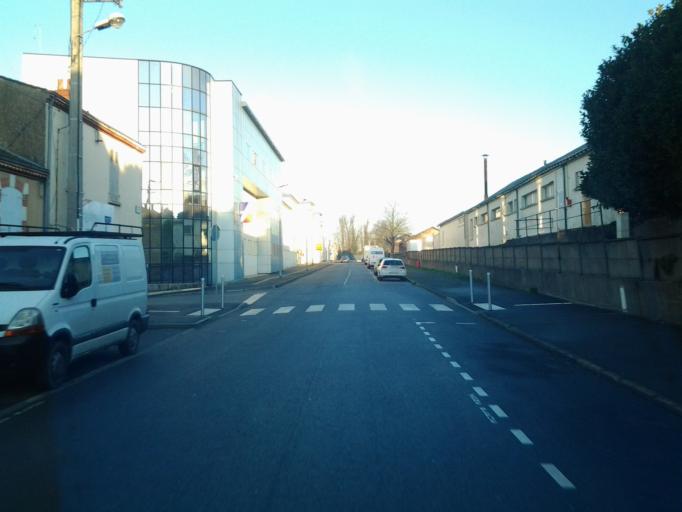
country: FR
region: Pays de la Loire
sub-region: Departement de la Vendee
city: La Roche-sur-Yon
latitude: 46.6694
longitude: -1.4365
